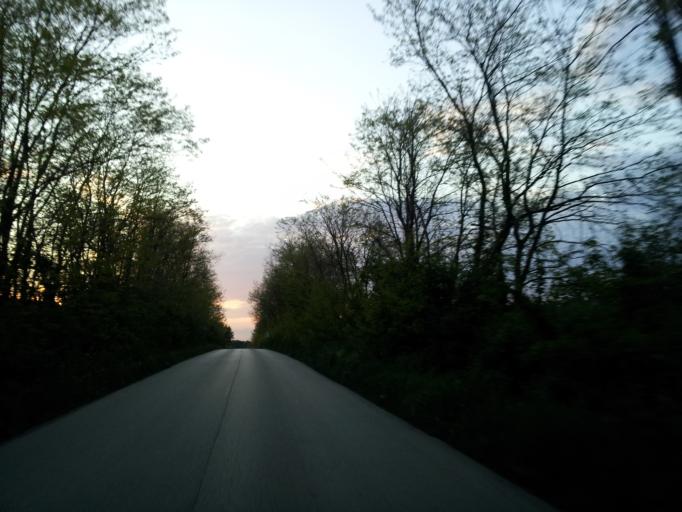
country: HU
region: Pest
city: Perbal
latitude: 47.6250
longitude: 18.7651
